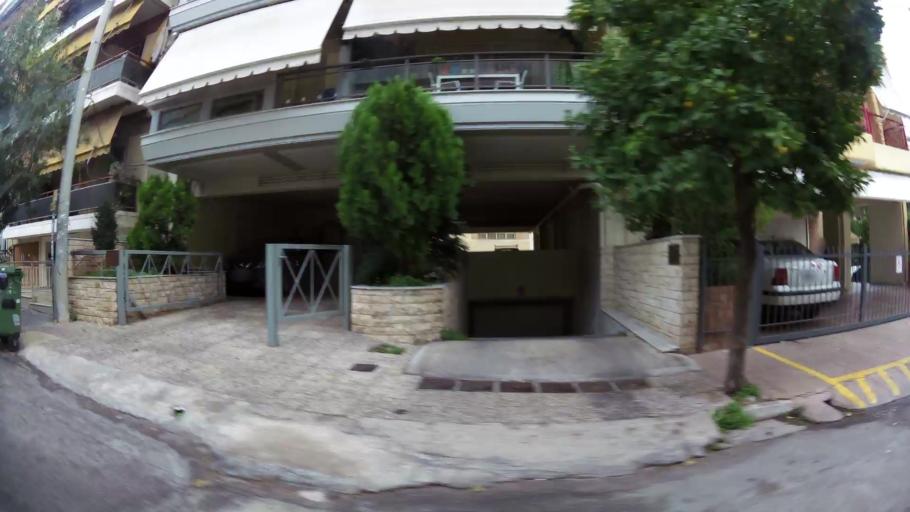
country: GR
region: Attica
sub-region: Nomarchia Athinas
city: Agia Varvara
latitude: 37.9784
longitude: 23.6630
